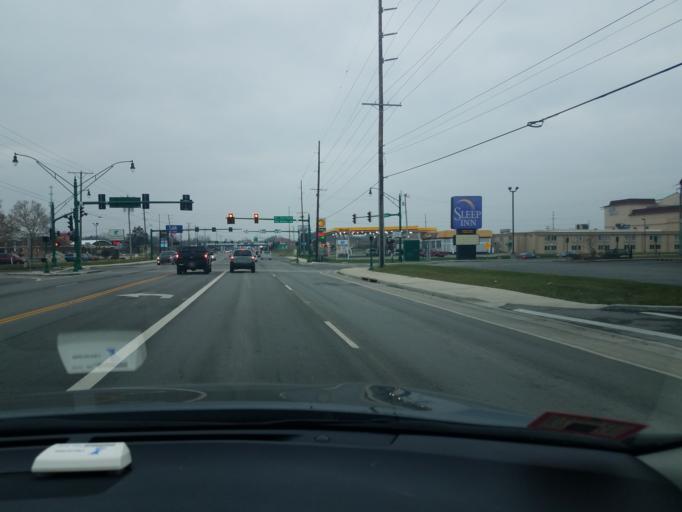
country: US
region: Ohio
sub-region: Erie County
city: Sandusky
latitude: 41.4033
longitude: -82.6591
